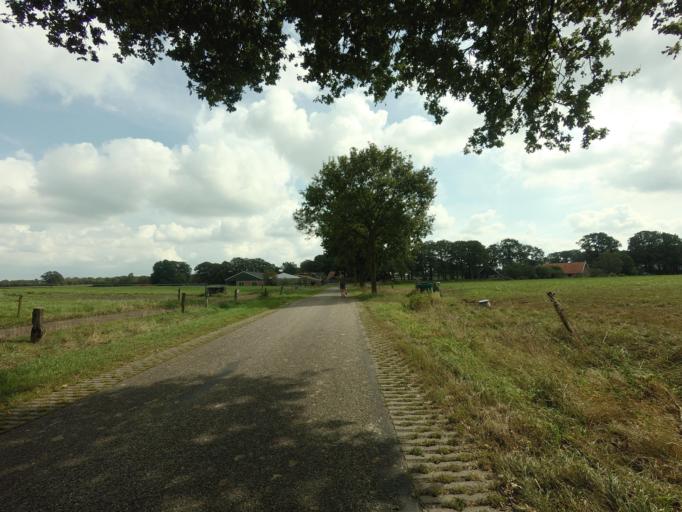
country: DE
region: Lower Saxony
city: Nordhorn
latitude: 52.3597
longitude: 7.0172
